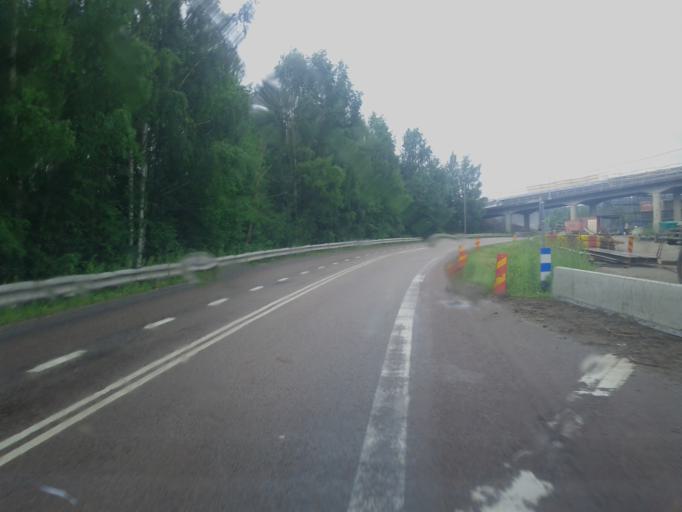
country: SE
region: Vaesternorrland
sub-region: Sundsvalls Kommun
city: Sundsvall
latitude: 62.4063
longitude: 17.2332
